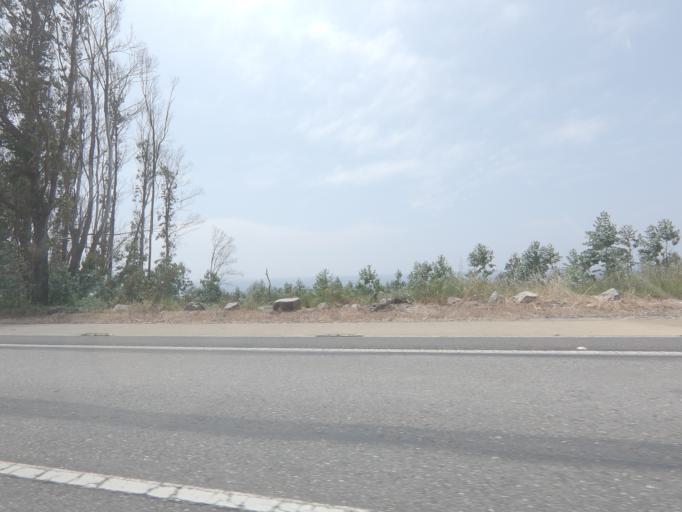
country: ES
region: Galicia
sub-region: Provincia de Pontevedra
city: A Guarda
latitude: 41.9338
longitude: -8.8834
